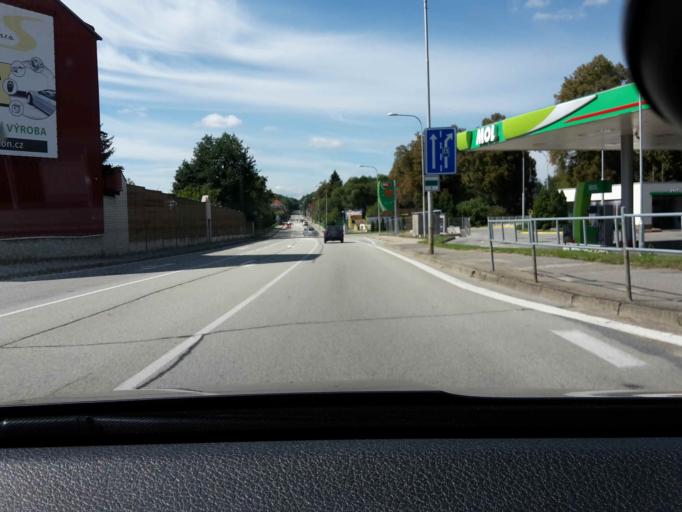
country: CZ
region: Jihocesky
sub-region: Okres Jindrichuv Hradec
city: Jindrichuv Hradec
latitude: 49.1541
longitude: 15.0027
